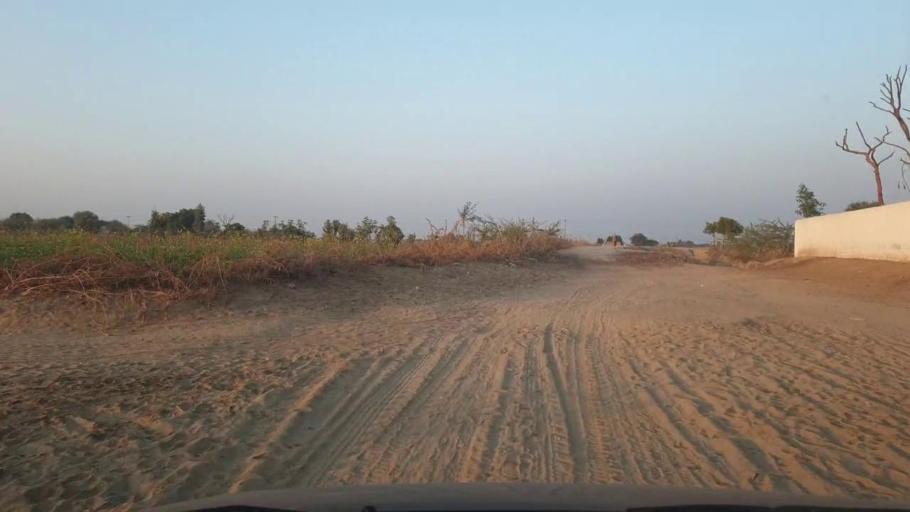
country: PK
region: Sindh
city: Bhit Shah
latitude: 25.8102
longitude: 68.5001
